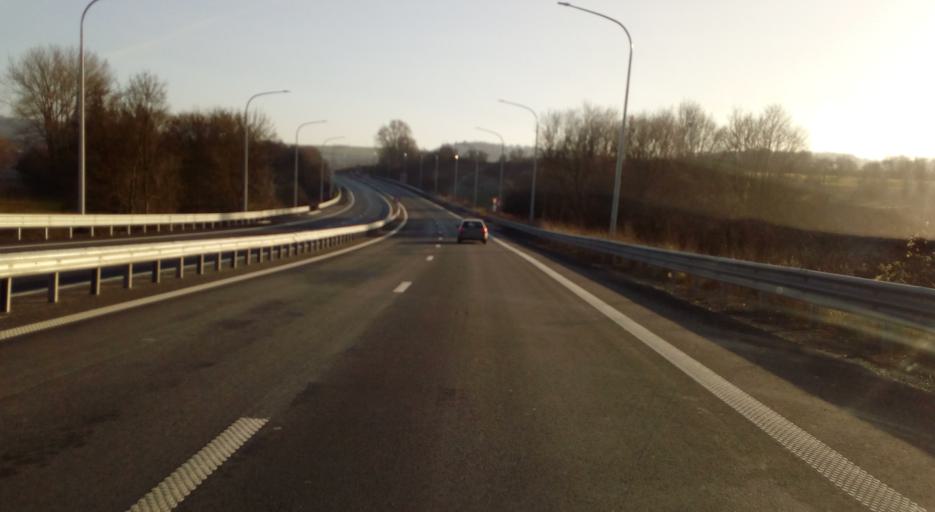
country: BE
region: Wallonia
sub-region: Province de Namur
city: Walcourt
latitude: 50.2835
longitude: 4.4820
